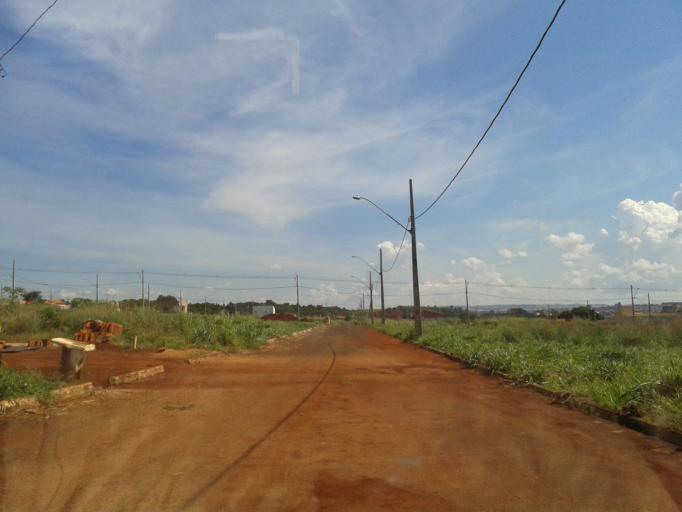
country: BR
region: Goias
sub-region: Itumbiara
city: Itumbiara
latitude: -18.4237
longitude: -49.1825
